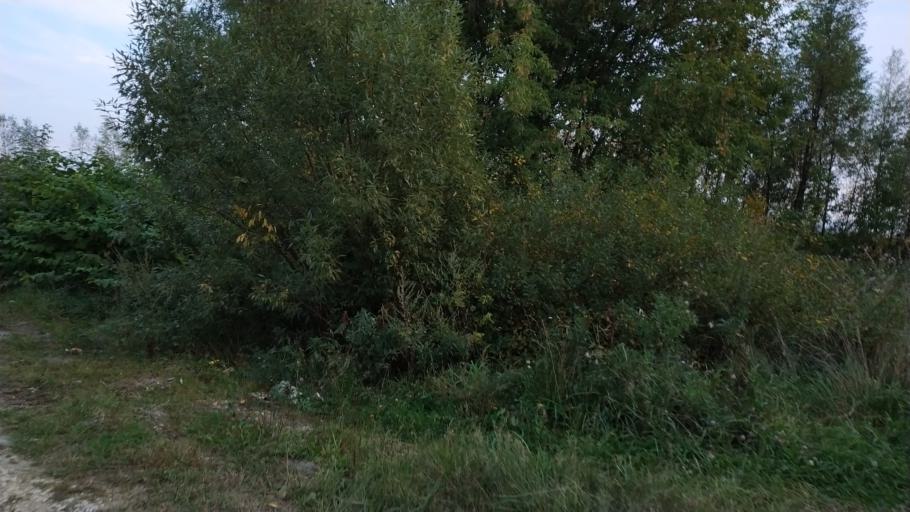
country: RU
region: Moscow
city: Solntsevo
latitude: 55.6390
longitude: 37.3723
